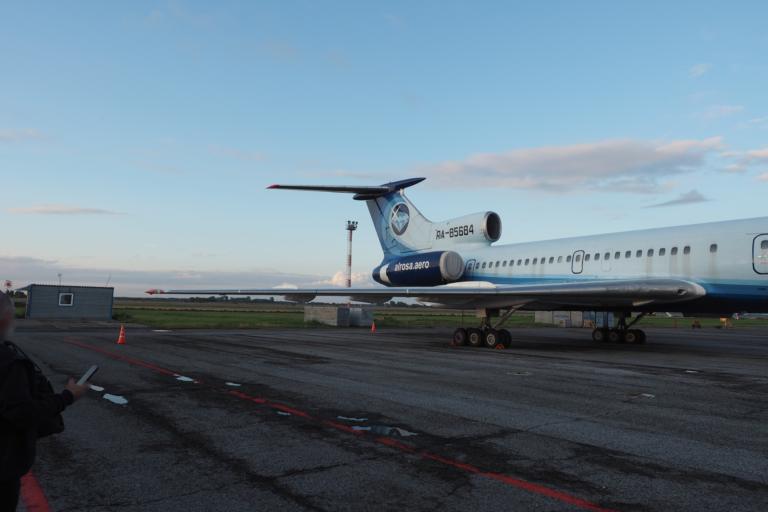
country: RU
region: Novosibirsk
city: Ob'
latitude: 55.0093
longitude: 82.6534
